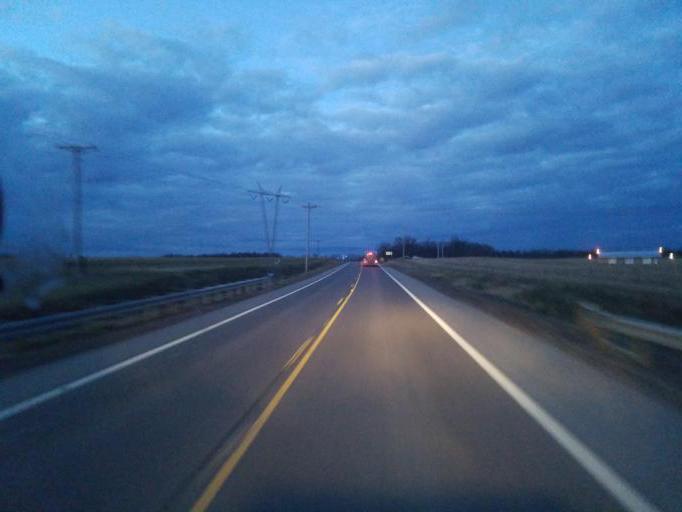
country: US
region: Ohio
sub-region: Knox County
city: Oak Hill
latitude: 40.3439
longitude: -82.3014
